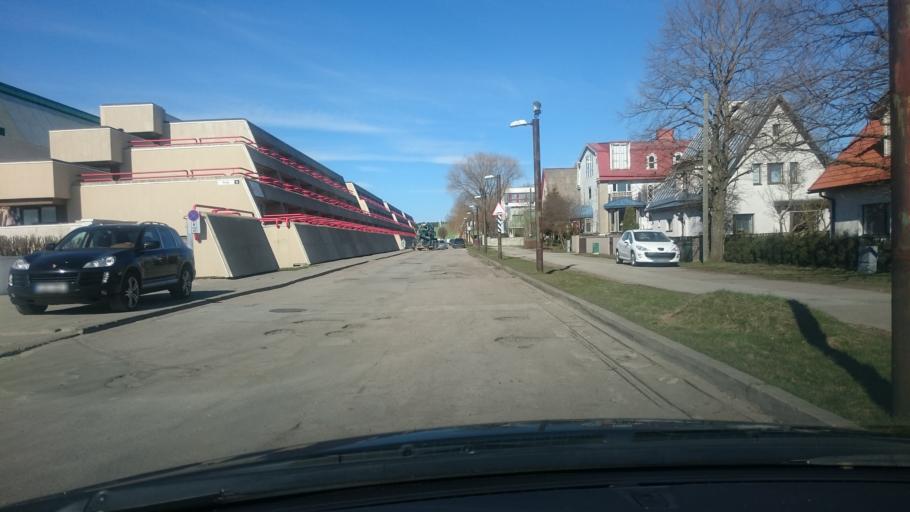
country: EE
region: Harju
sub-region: Viimsi vald
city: Viimsi
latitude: 59.4635
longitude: 24.8223
